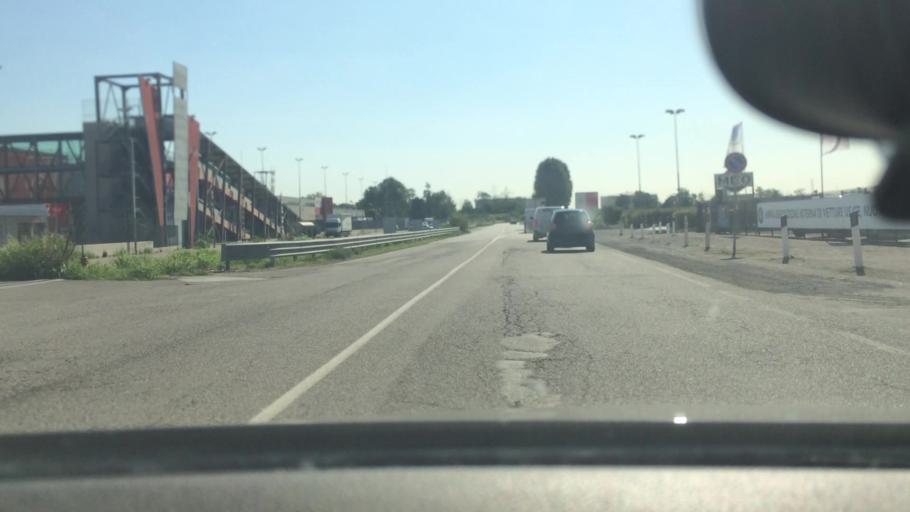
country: IT
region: Lombardy
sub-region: Citta metropolitana di Milano
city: Santo Stefano Ticino
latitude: 45.5030
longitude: 8.9106
